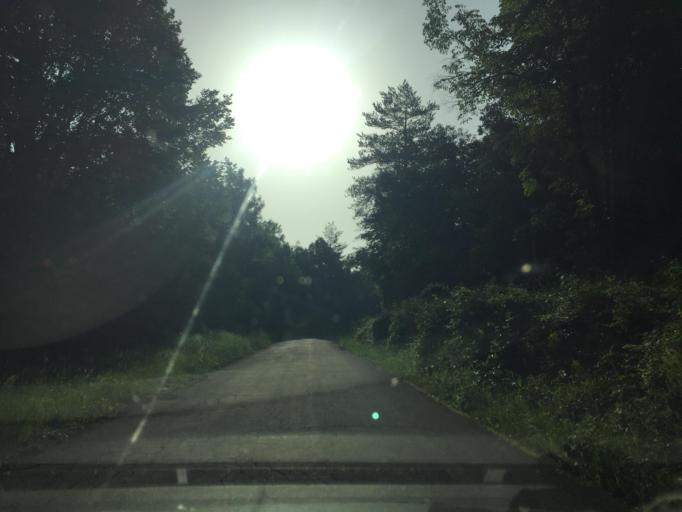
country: HR
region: Istarska
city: Buzet
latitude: 45.4625
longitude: 14.1296
